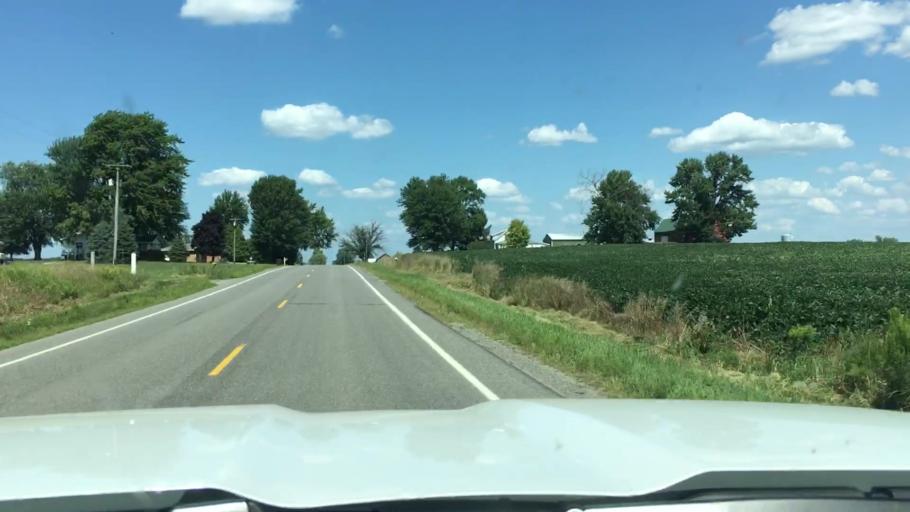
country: US
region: Michigan
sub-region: Muskegon County
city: Ravenna
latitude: 43.1702
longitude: -85.9877
